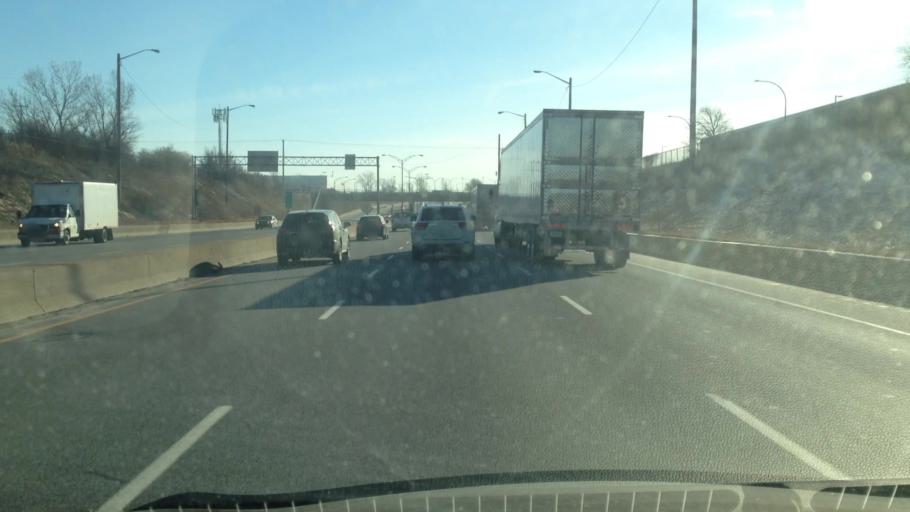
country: CA
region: Quebec
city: Cote-Saint-Luc
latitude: 45.4694
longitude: -73.7015
